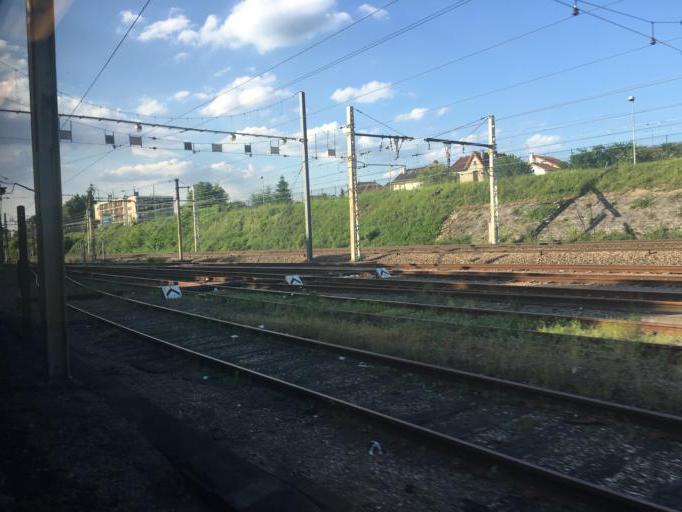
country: FR
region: Ile-de-France
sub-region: Departement de Seine-et-Marne
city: Combs-la-Ville
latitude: 48.6624
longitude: 2.5516
